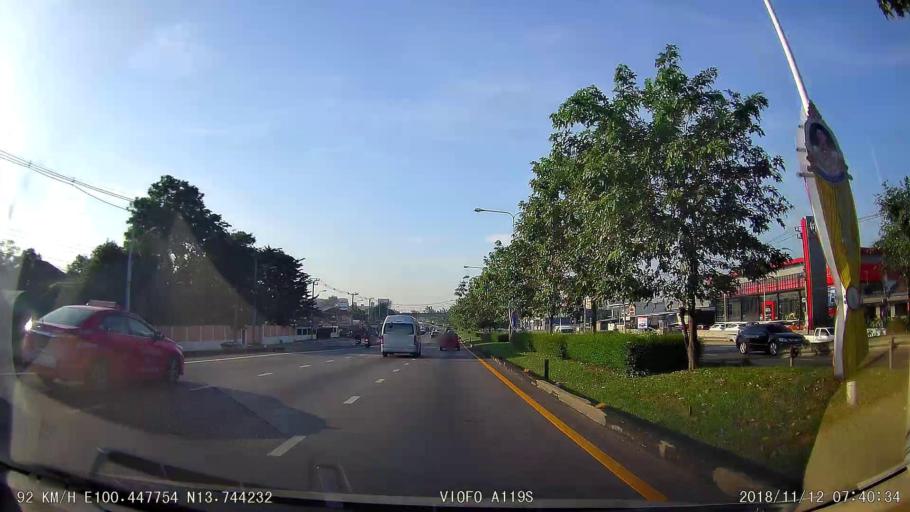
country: TH
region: Bangkok
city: Phasi Charoen
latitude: 13.7440
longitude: 100.4477
